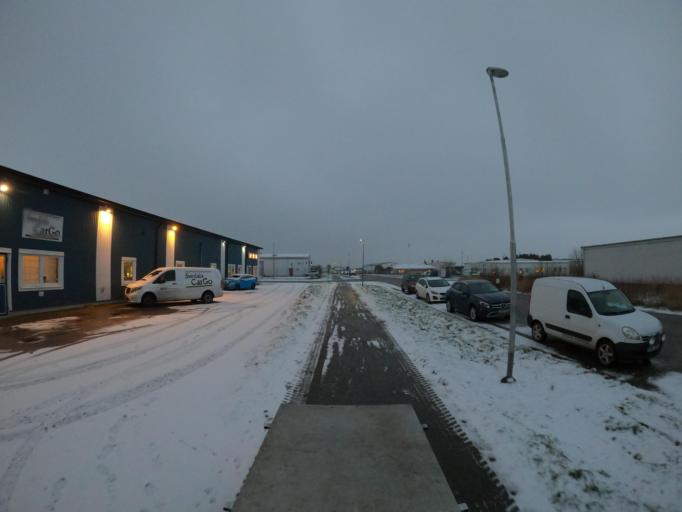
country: SE
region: Skane
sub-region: Svedala Kommun
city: Svedala
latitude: 55.5123
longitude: 13.2561
